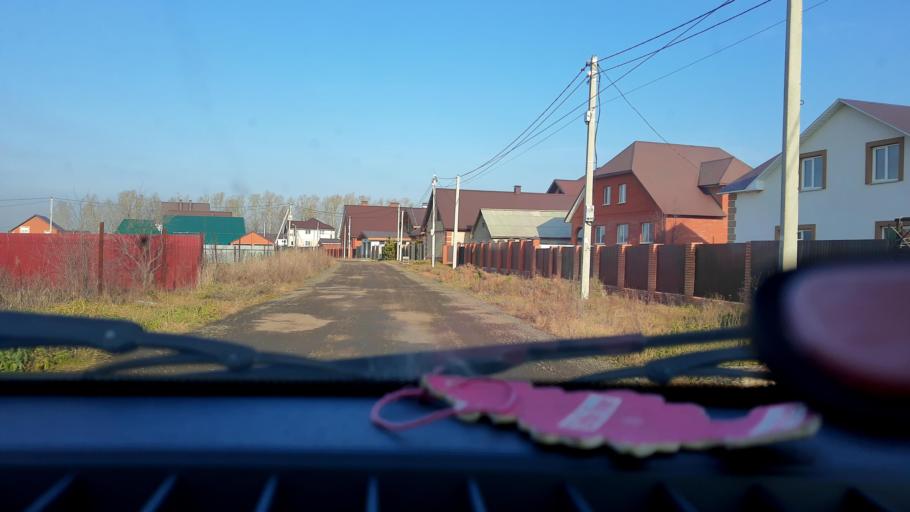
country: RU
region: Bashkortostan
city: Ufa
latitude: 54.6786
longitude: 56.0908
